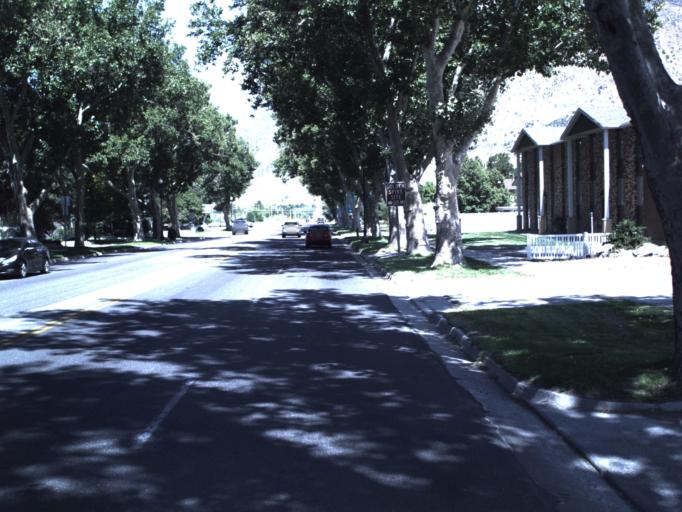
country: US
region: Utah
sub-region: Box Elder County
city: Brigham City
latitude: 41.5251
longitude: -112.0154
